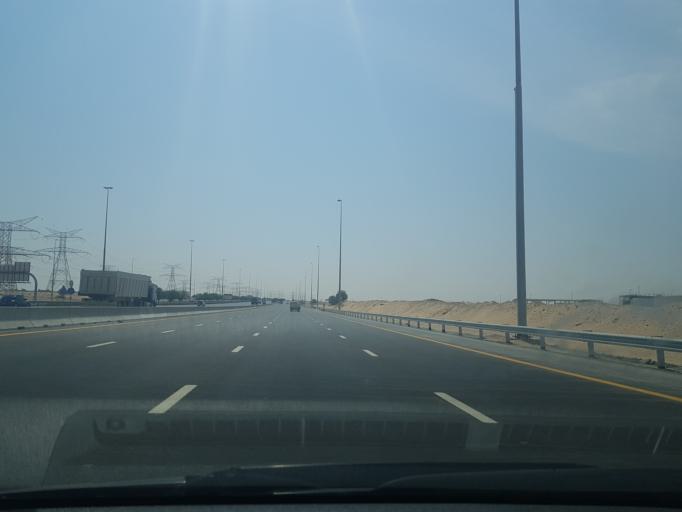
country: AE
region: Ash Shariqah
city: Sharjah
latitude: 25.2323
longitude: 55.5630
